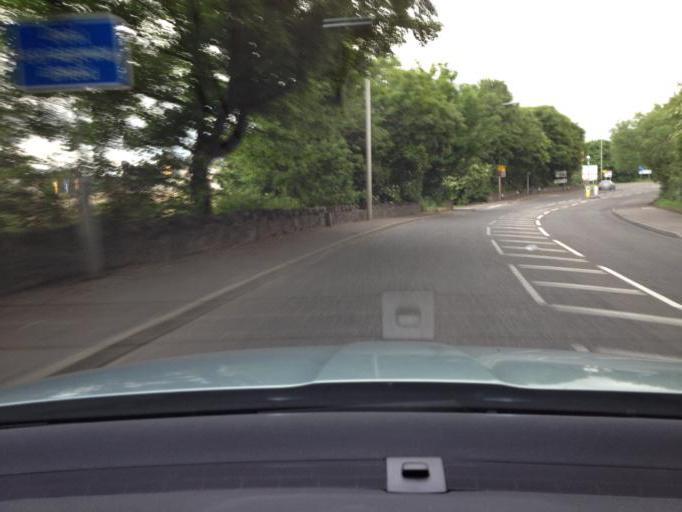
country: GB
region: Scotland
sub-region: Perth and Kinross
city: Perth
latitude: 56.3740
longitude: -3.4250
